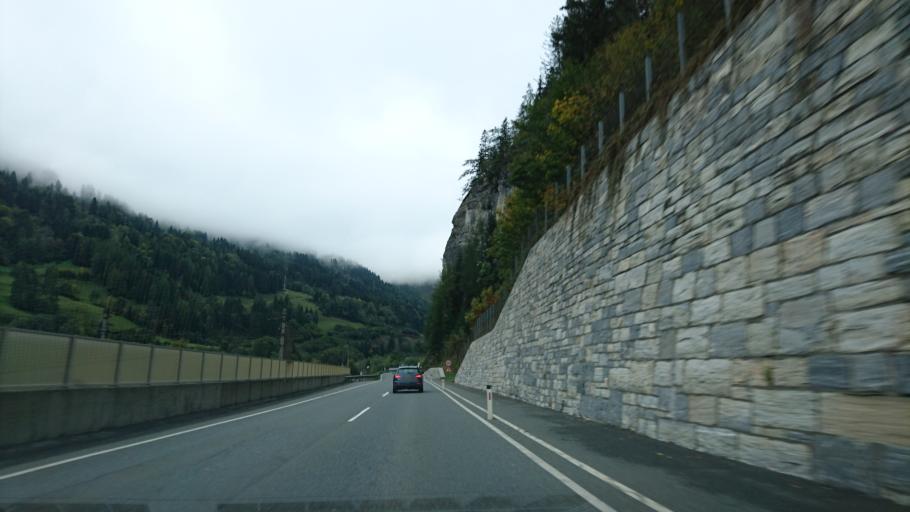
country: AT
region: Salzburg
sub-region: Politischer Bezirk Sankt Johann im Pongau
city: Dorfgastein
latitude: 47.2625
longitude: 13.0852
